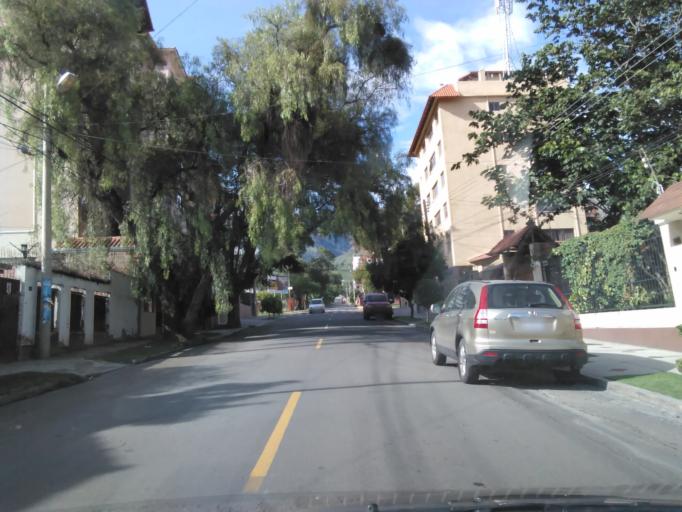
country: BO
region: Cochabamba
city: Cochabamba
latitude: -17.3721
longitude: -66.1465
